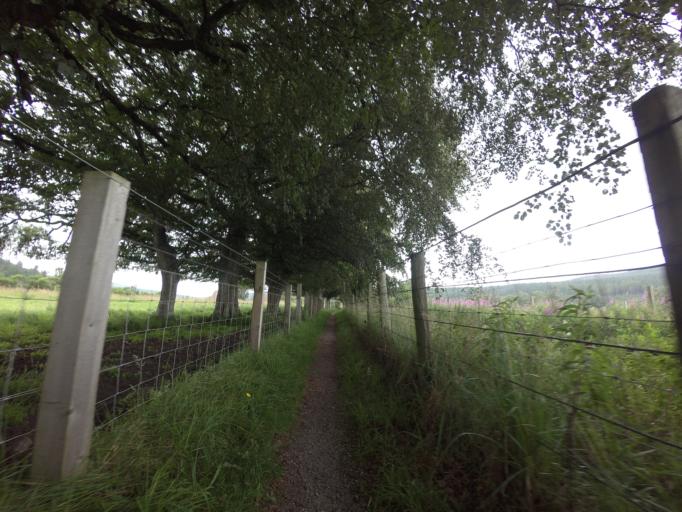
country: GB
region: Scotland
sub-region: Highland
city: Evanton
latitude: 57.9220
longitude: -4.4040
